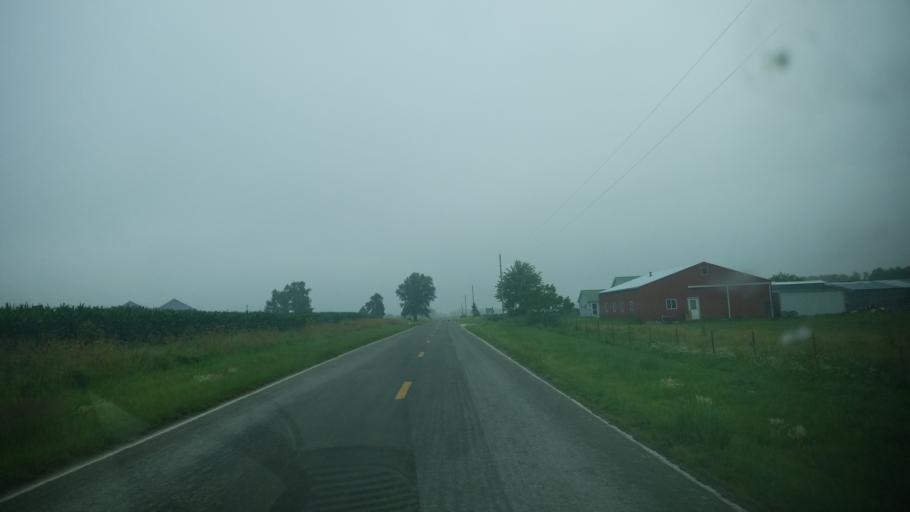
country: US
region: Missouri
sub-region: Audrain County
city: Vandalia
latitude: 39.3277
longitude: -91.3451
